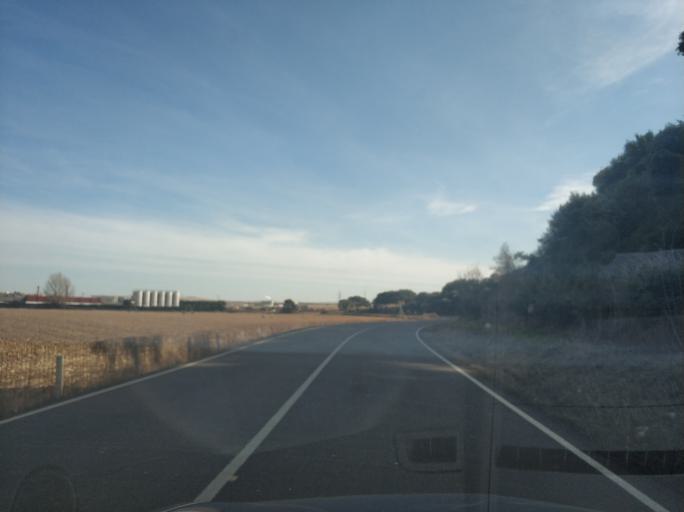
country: ES
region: Castille and Leon
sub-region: Provincia de Salamanca
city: Carrascal de Barregas
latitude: 40.9912
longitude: -5.7326
